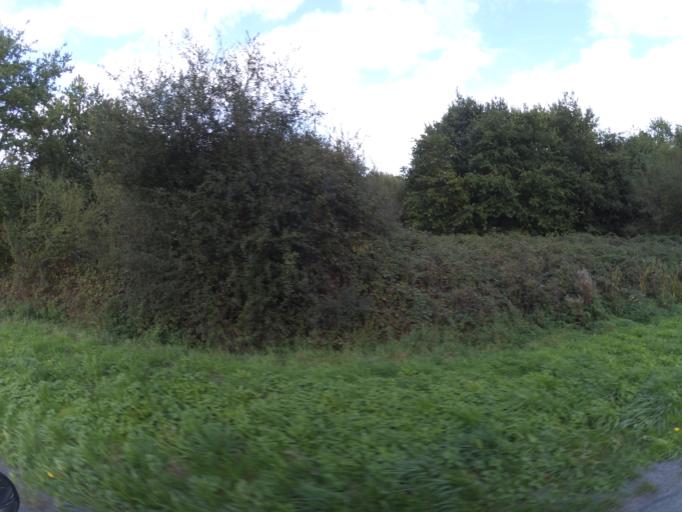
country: FR
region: Pays de la Loire
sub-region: Departement de la Loire-Atlantique
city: Fegreac
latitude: 47.6060
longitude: -2.0318
